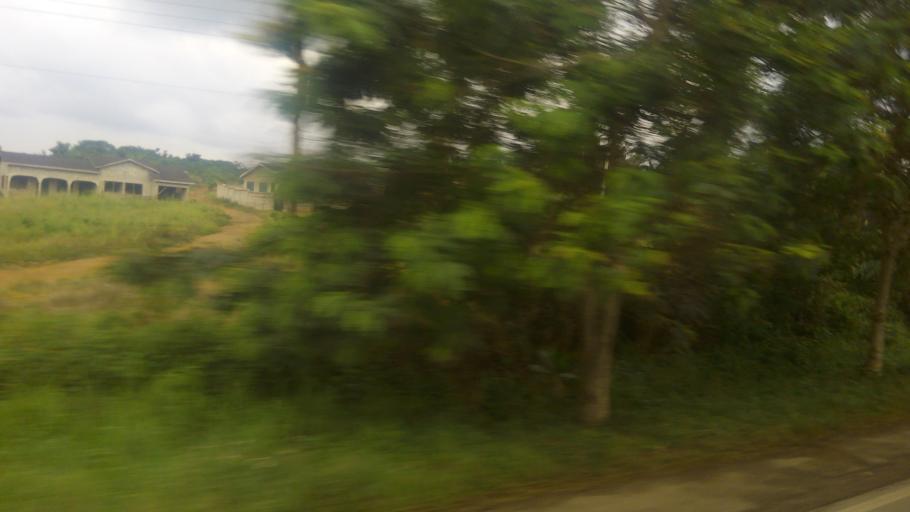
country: GH
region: Western
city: Takoradi
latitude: 4.8953
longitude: -1.9354
